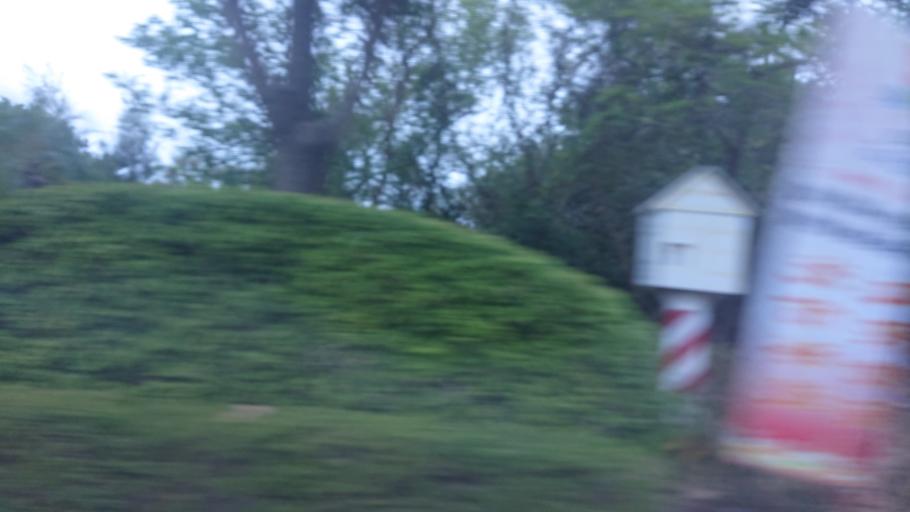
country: TW
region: Fukien
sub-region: Kinmen
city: Jincheng
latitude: 24.4108
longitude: 118.3000
